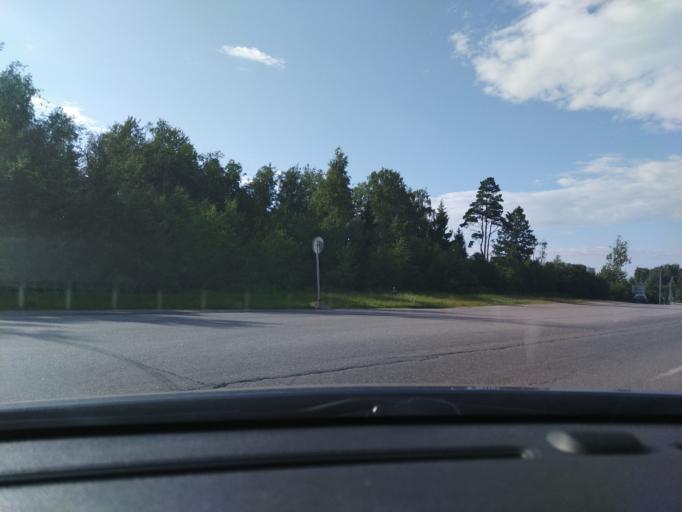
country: RU
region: St.-Petersburg
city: Gorelovo
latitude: 59.7809
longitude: 30.1700
